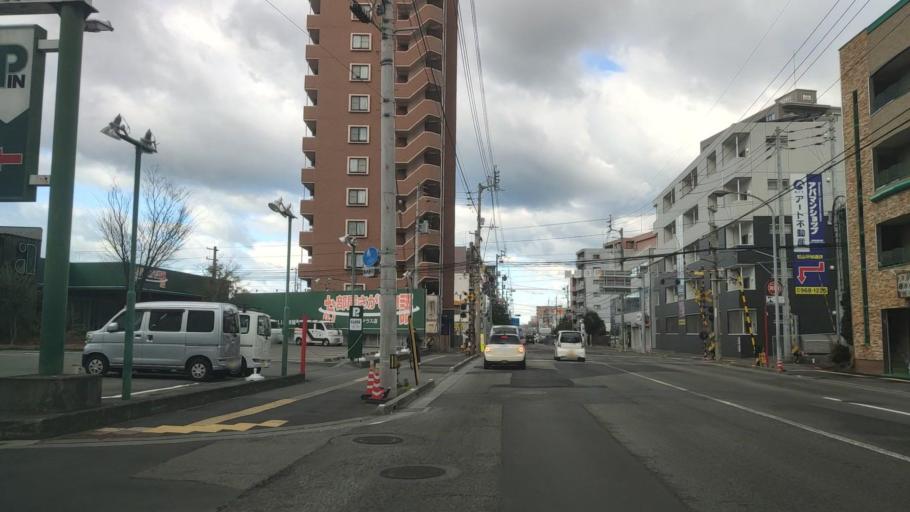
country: JP
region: Ehime
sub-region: Shikoku-chuo Shi
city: Matsuyama
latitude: 33.8530
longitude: 132.7571
